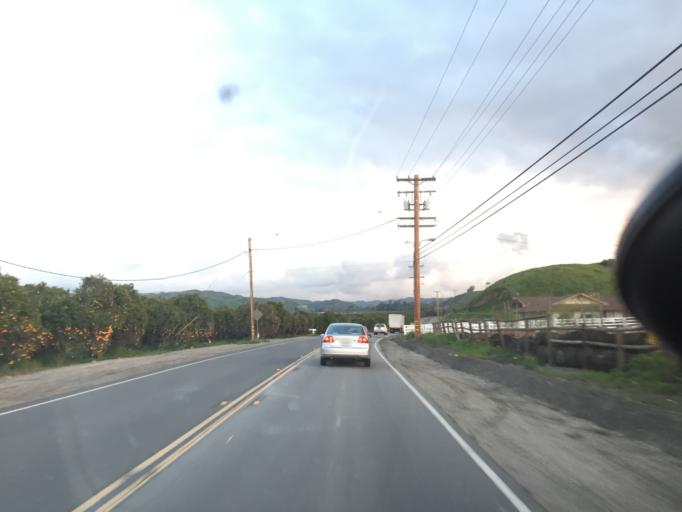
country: US
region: California
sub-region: San Bernardino County
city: Redlands
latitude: 34.0179
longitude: -117.1880
